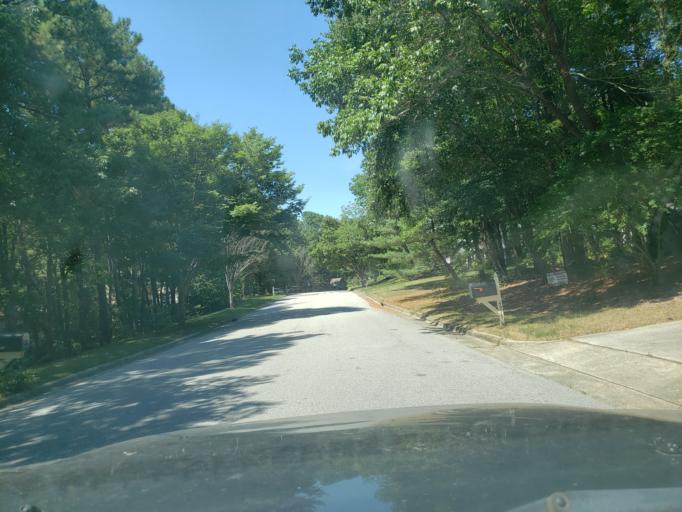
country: US
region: North Carolina
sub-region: Durham County
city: Durham
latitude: 35.9138
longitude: -78.9461
